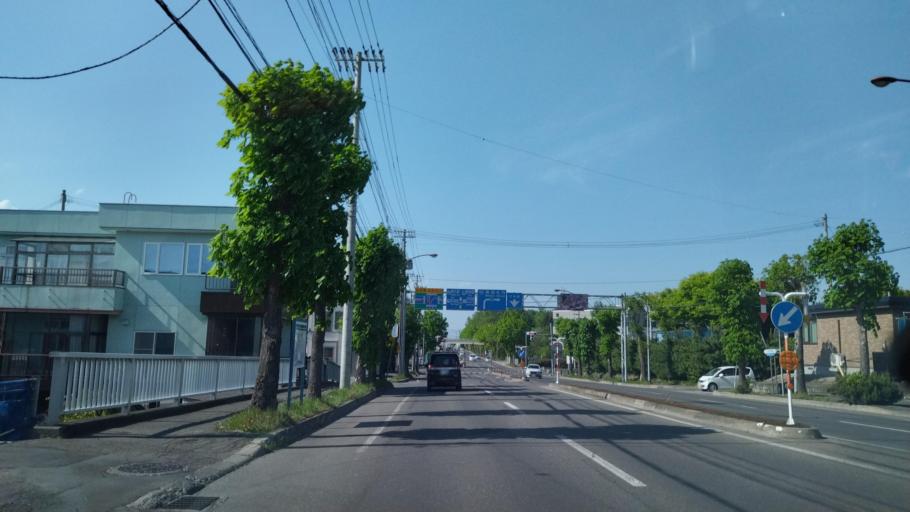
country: JP
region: Hokkaido
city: Obihiro
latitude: 42.8964
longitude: 143.1814
